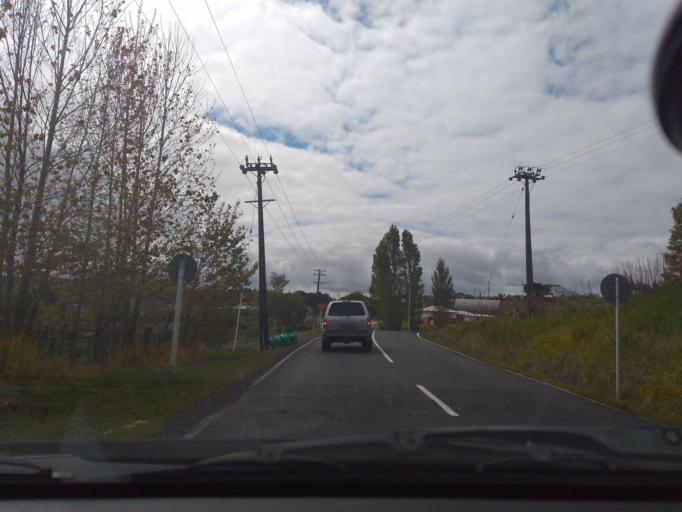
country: NZ
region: Auckland
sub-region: Auckland
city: Muriwai Beach
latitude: -36.8515
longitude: 174.5355
